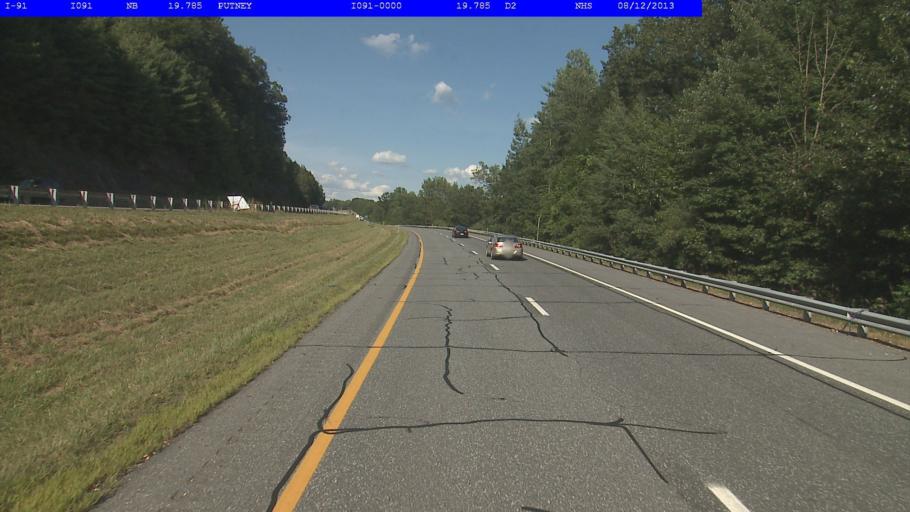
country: US
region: New Hampshire
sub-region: Cheshire County
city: Westmoreland
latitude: 42.9710
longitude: -72.4901
